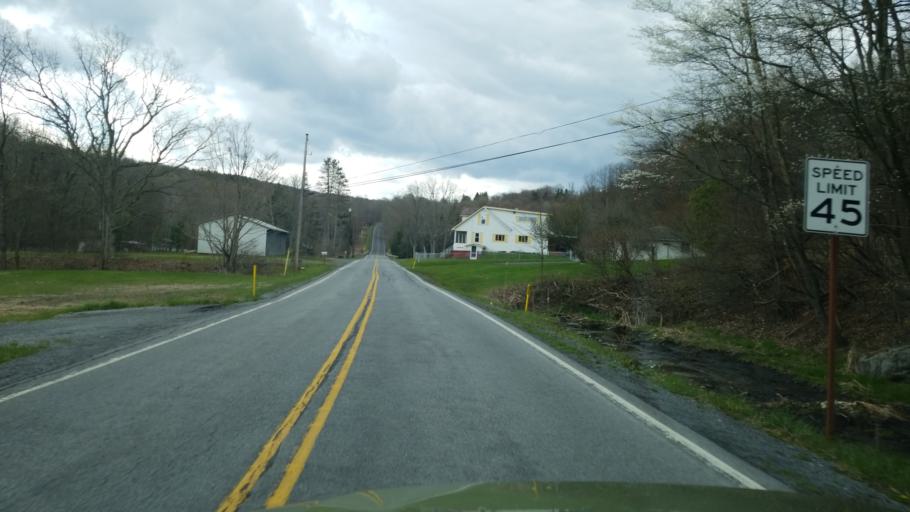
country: US
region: Pennsylvania
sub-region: Clearfield County
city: Curwensville
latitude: 40.8839
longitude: -78.4592
